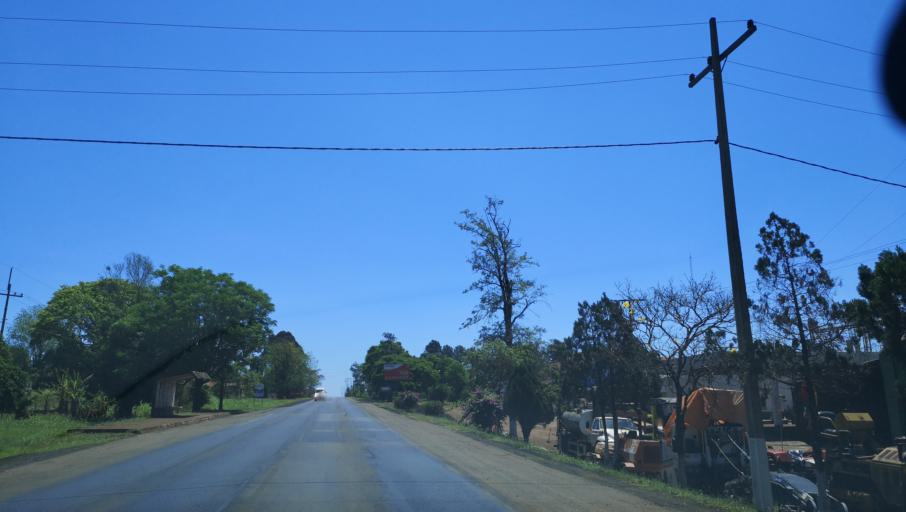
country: PY
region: Itapua
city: San Juan del Parana
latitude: -27.2470
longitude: -55.9934
